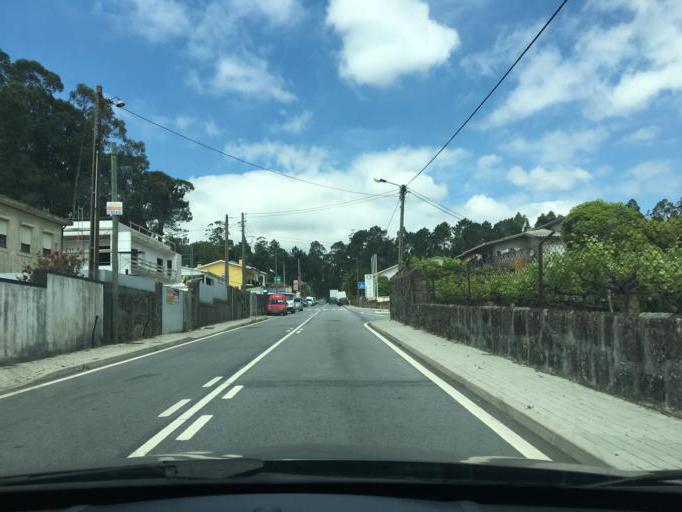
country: PT
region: Porto
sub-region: Maia
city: Anta
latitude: 41.2874
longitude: -8.6044
